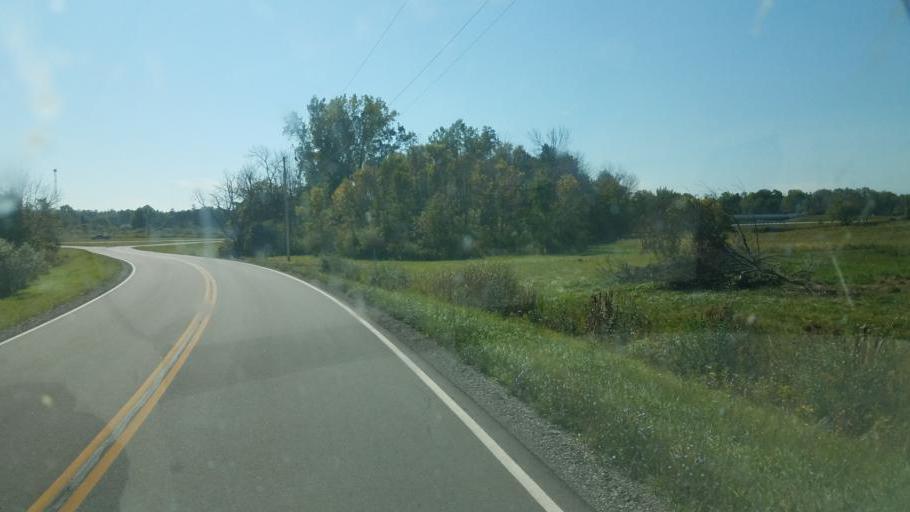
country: US
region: Ohio
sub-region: Richland County
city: Ontario
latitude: 40.7640
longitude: -82.6094
